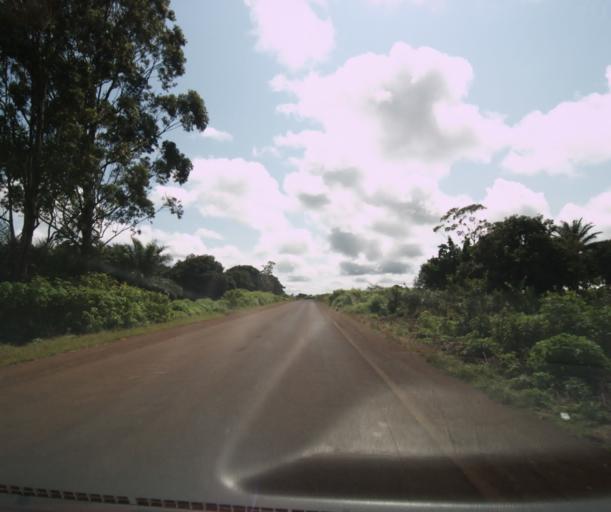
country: CM
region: West
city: Foumban
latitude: 5.6723
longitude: 10.7926
